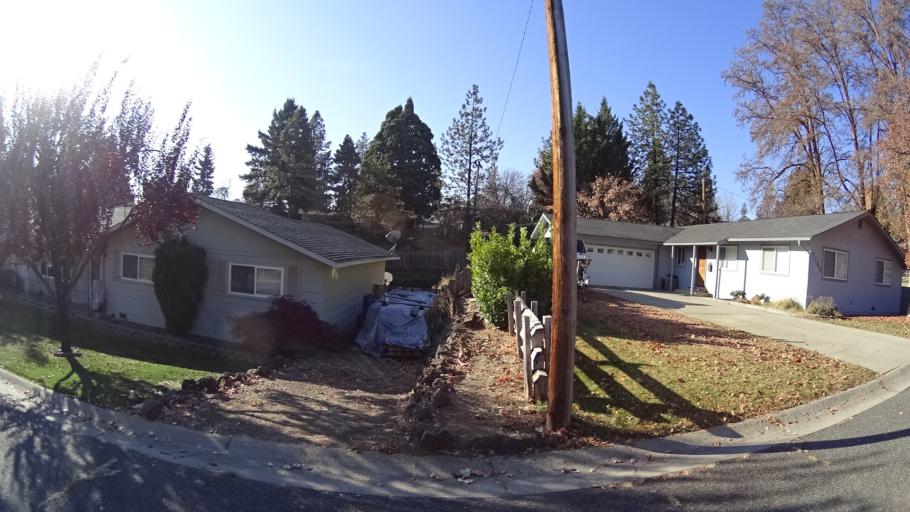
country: US
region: California
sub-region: Siskiyou County
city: Yreka
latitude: 41.7406
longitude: -122.6491
